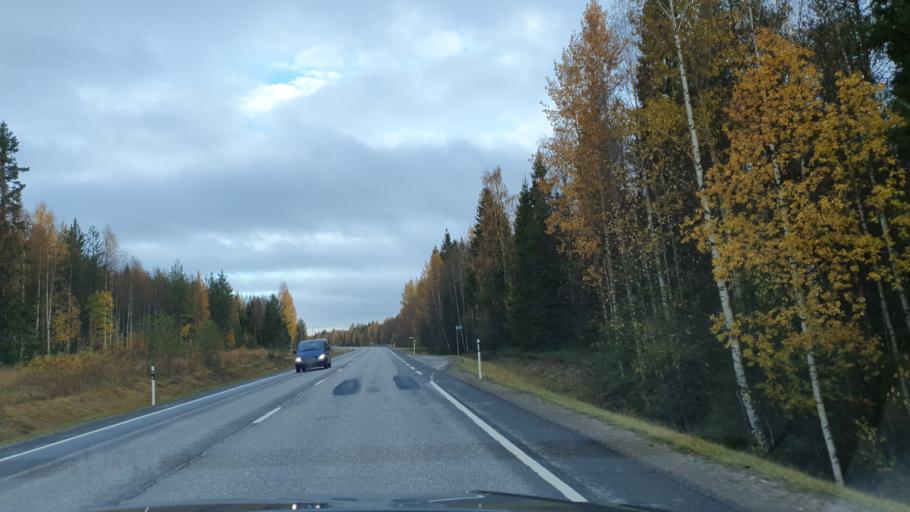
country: FI
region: Lapland
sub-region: Rovaniemi
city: Rovaniemi
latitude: 66.5703
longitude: 25.6357
